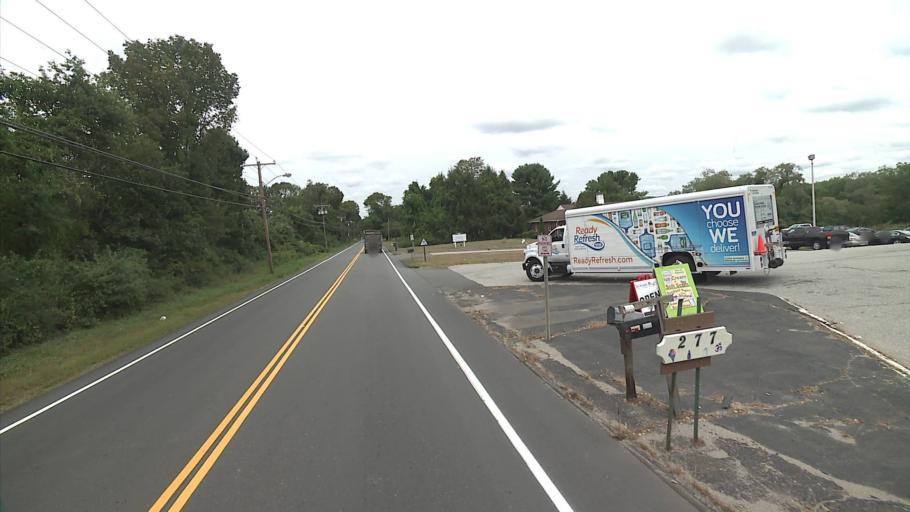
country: US
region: Connecticut
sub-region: Tolland County
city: Hebron
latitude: 41.6415
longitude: -72.3553
